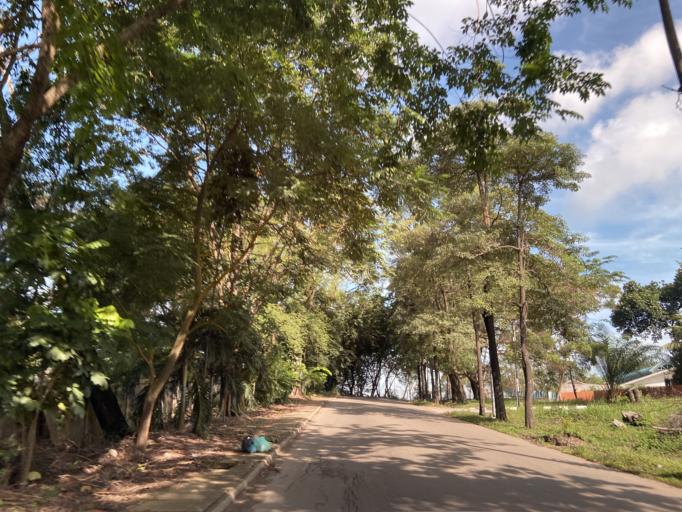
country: SG
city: Singapore
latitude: 1.1747
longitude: 104.0107
